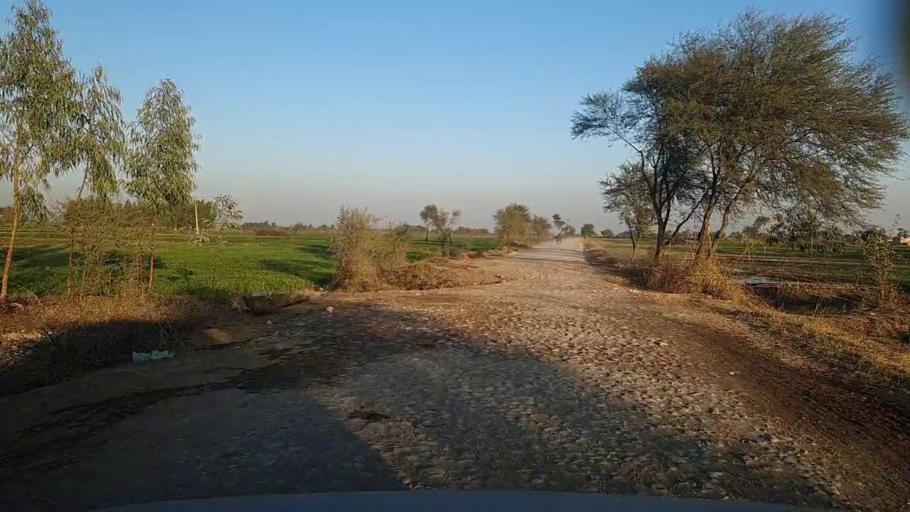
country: PK
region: Sindh
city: Khairpur
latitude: 27.9159
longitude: 69.6833
